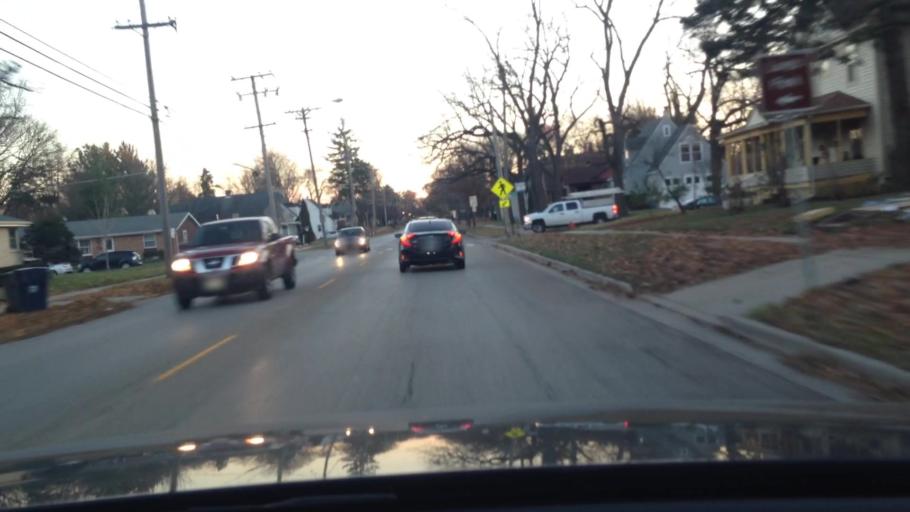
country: US
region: Illinois
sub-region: Kane County
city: Elgin
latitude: 42.0434
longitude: -88.2677
